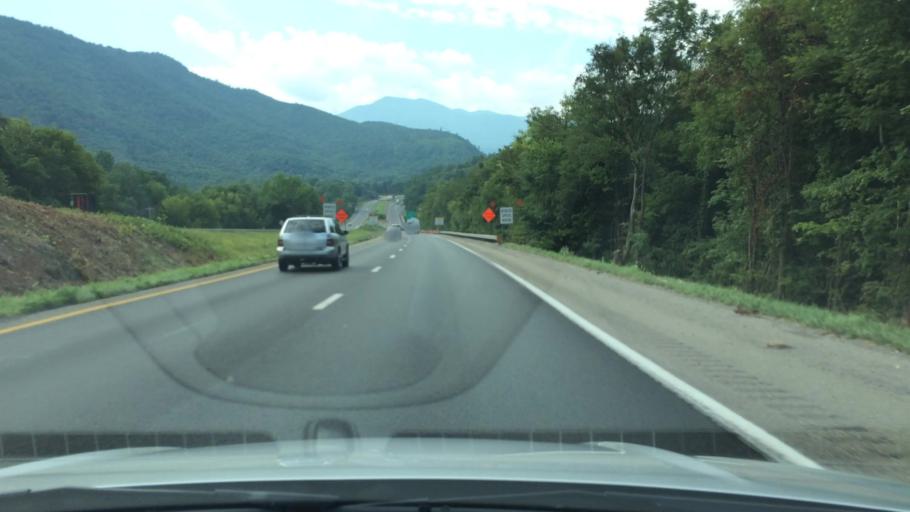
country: US
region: Tennessee
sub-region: Cocke County
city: Newport
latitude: 35.8478
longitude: -83.1832
